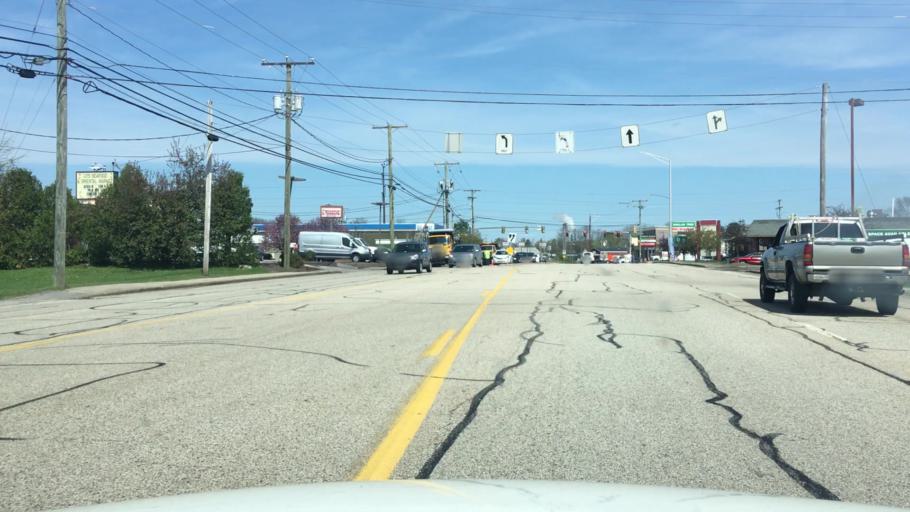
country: US
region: Maine
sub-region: York County
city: South Eliot
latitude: 43.0928
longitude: -70.7932
